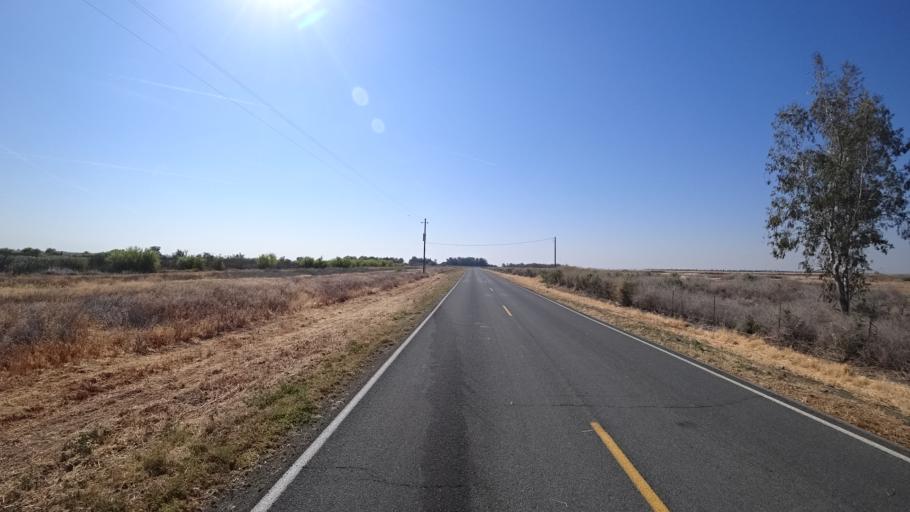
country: US
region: California
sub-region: Fresno County
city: Riverdale
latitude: 36.3731
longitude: -119.9249
